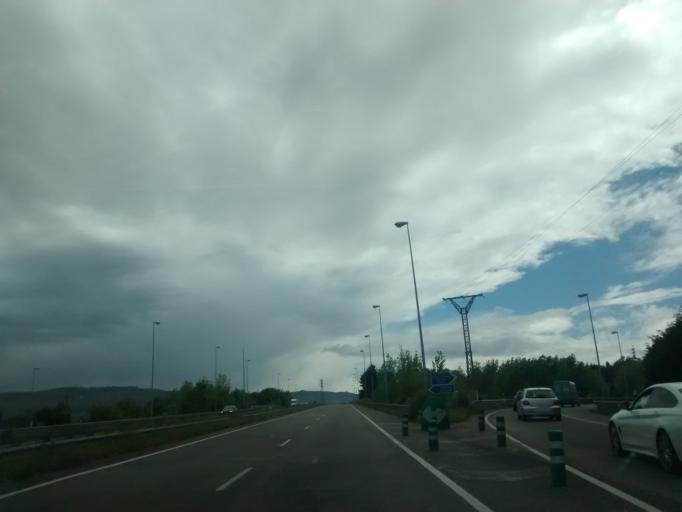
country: ES
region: Asturias
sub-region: Province of Asturias
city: Gijon
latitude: 43.5239
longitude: -5.6391
